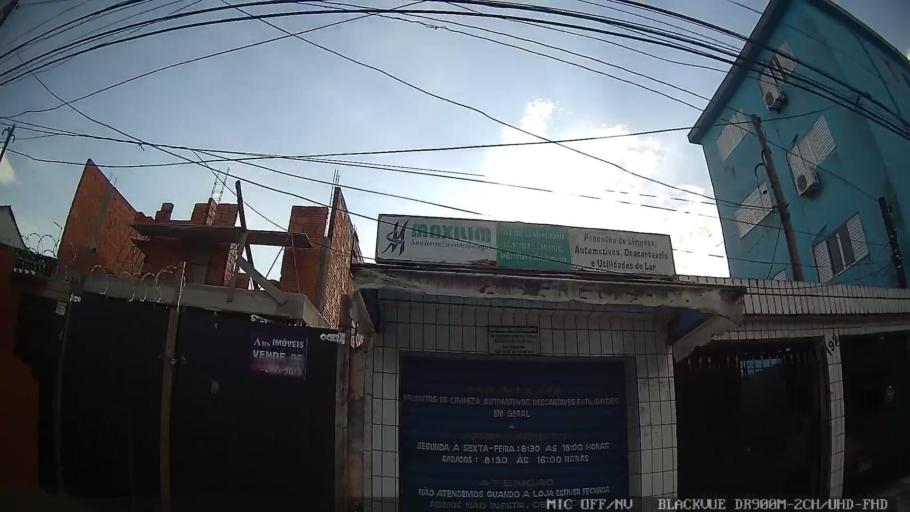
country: BR
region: Sao Paulo
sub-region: Cubatao
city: Cubatao
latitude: -23.8933
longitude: -46.4221
